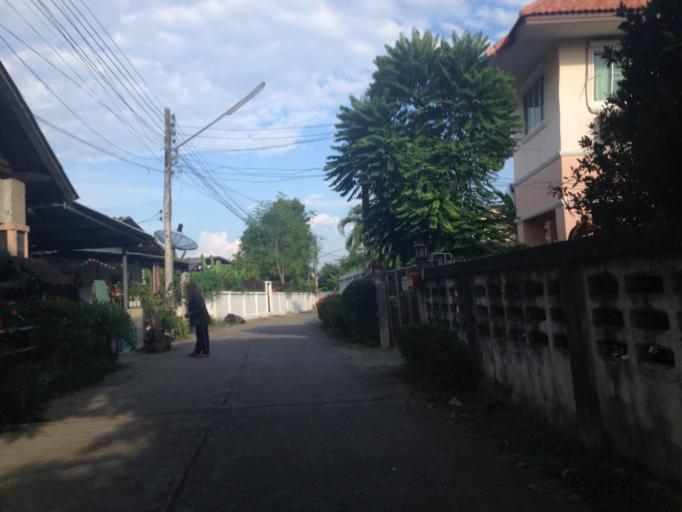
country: TH
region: Chiang Mai
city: Hang Dong
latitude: 18.7238
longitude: 98.9243
